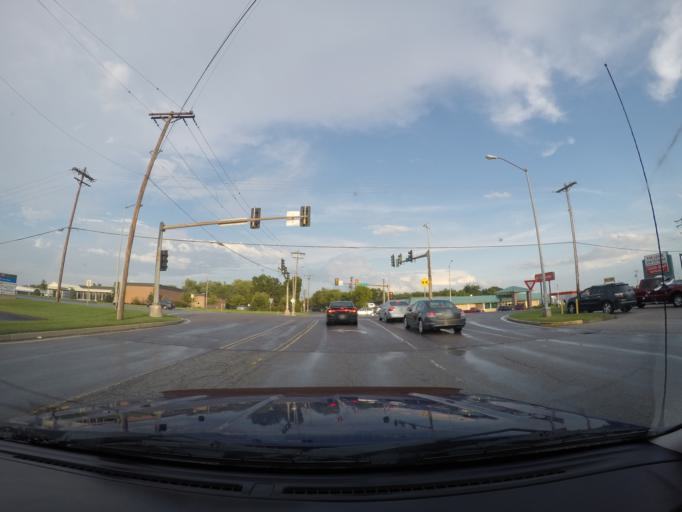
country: US
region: Missouri
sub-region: Saint Louis County
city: Sunset Hills
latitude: 38.5511
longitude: -90.4075
